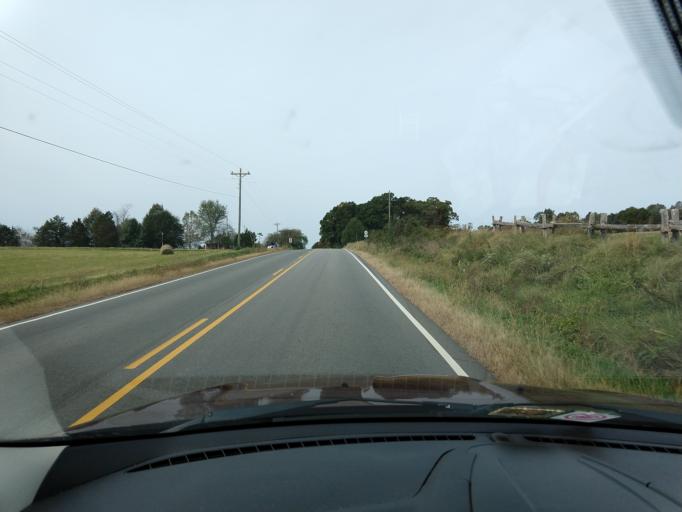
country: US
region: Virginia
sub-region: Franklin County
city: Union Hall
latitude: 36.9657
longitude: -79.5853
